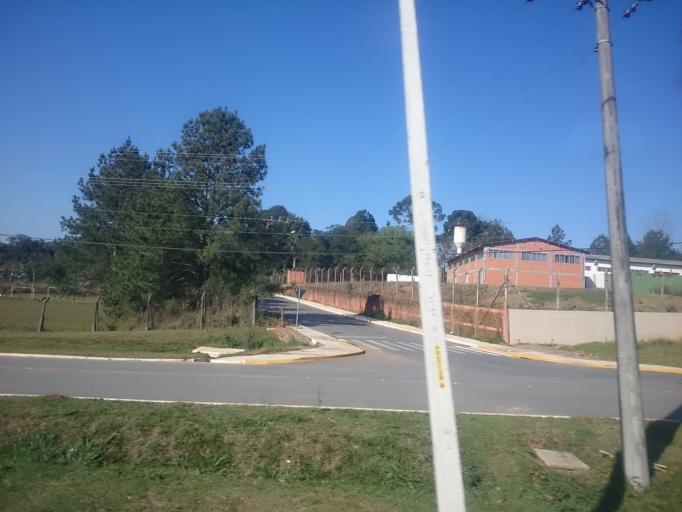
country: BR
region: Parana
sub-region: Rio Negro
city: Rio Negro
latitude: -26.0955
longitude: -49.7804
